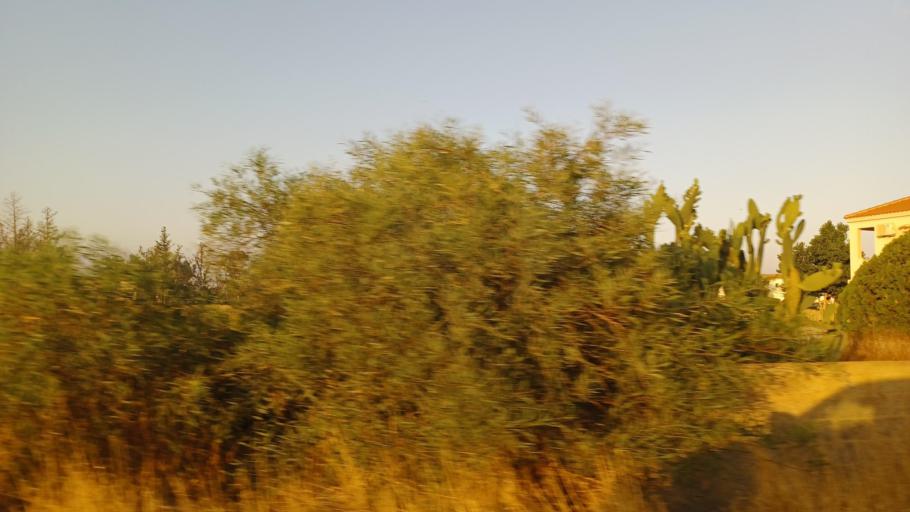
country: CY
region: Ammochostos
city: Avgorou
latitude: 35.0340
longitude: 33.8475
